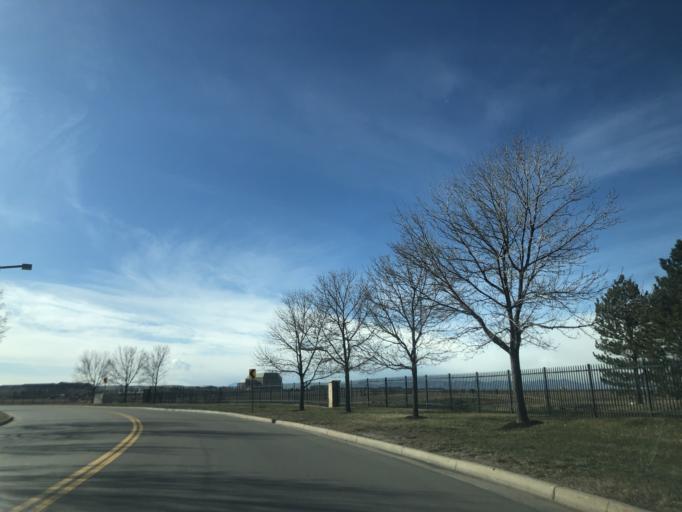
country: US
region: Colorado
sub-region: Douglas County
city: Meridian
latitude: 39.5553
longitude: -104.8461
